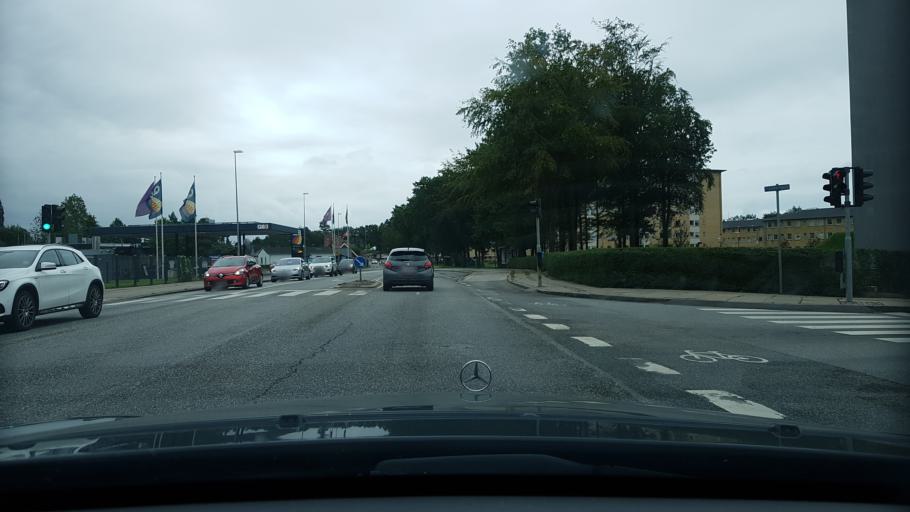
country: DK
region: Central Jutland
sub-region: Randers Kommune
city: Randers
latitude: 56.4802
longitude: 10.0414
